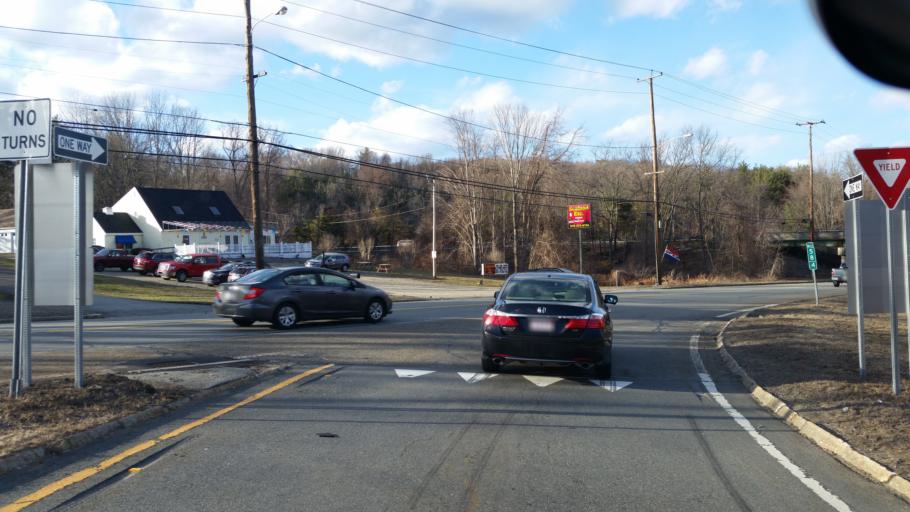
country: US
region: Massachusetts
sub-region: Essex County
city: Haverhill
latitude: 42.8014
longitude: -71.0528
